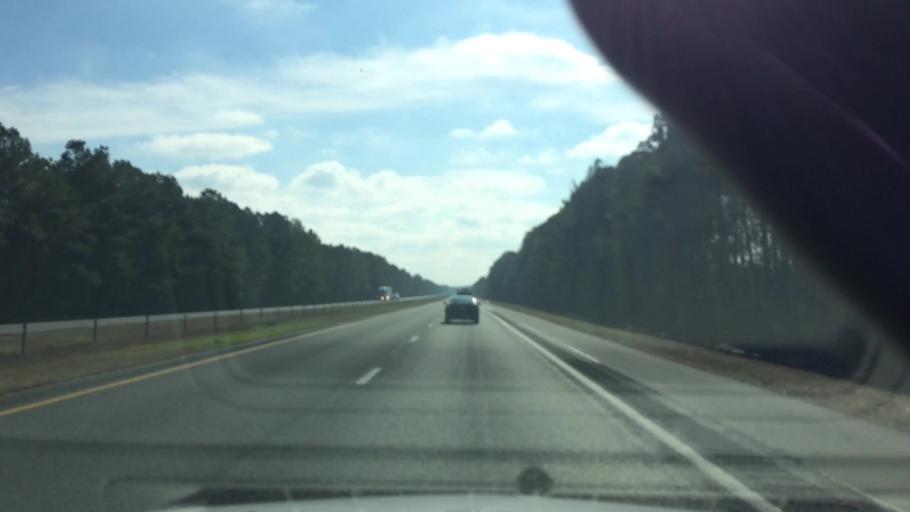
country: US
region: North Carolina
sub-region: Duplin County
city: Wallace
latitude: 34.7275
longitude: -77.9442
